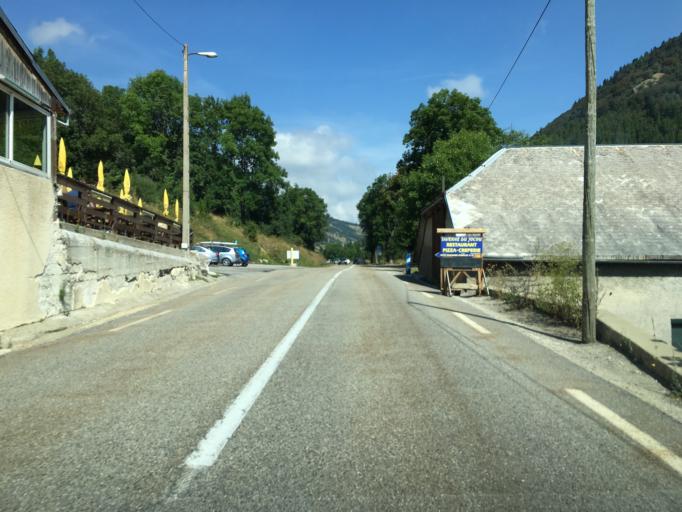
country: FR
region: Rhone-Alpes
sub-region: Departement de l'Isere
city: Mens
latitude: 44.7008
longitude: 5.6819
